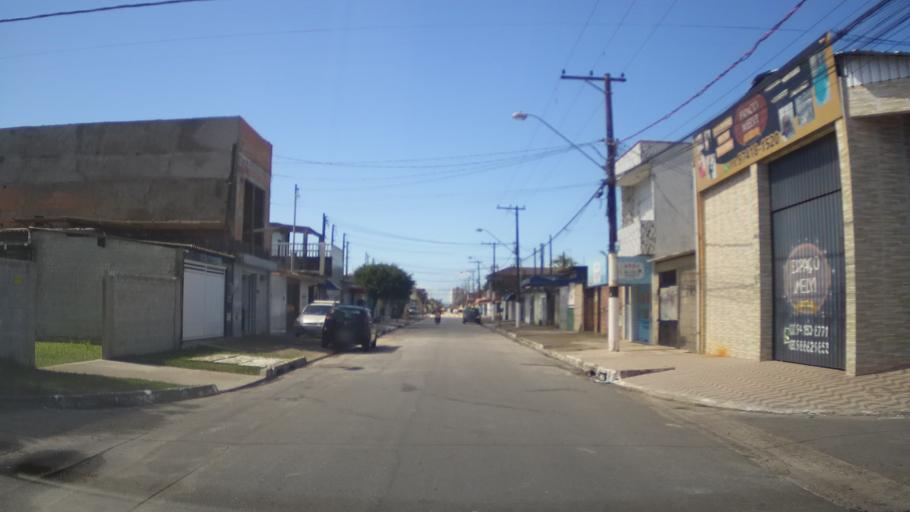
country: BR
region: Sao Paulo
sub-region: Mongagua
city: Mongagua
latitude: -24.0351
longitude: -46.5328
